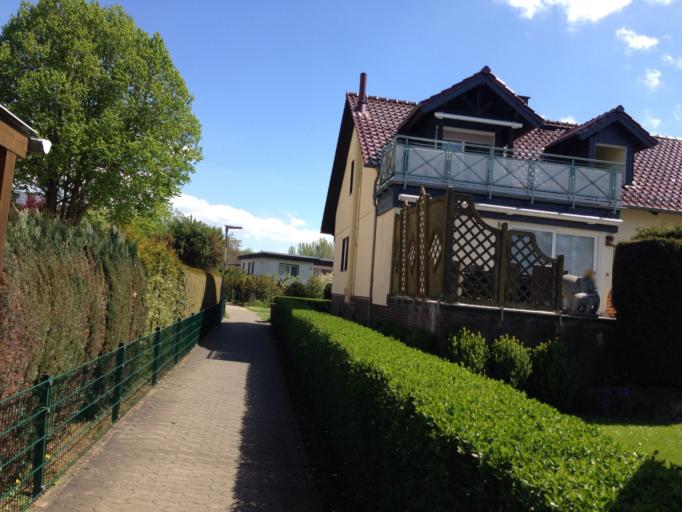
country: DE
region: Hesse
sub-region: Regierungsbezirk Giessen
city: Lich
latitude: 50.5159
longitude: 8.8098
